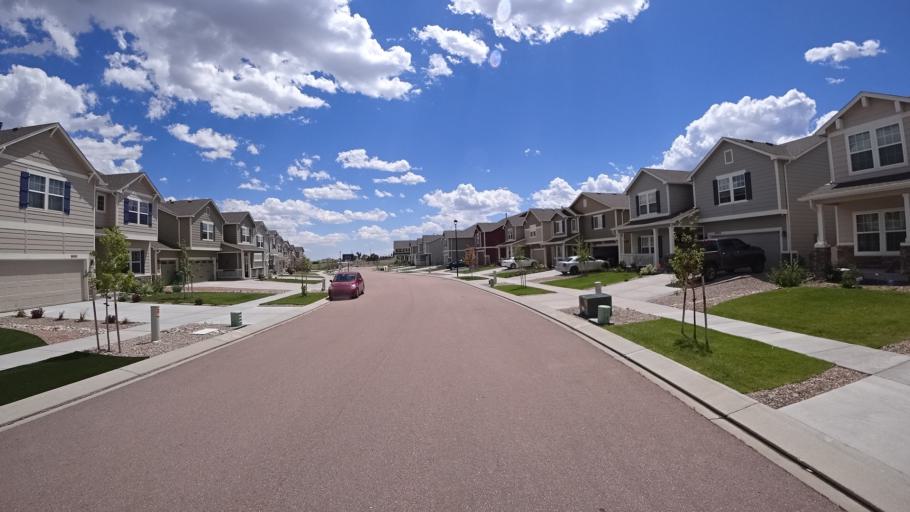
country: US
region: Colorado
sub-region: El Paso County
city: Black Forest
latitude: 38.9503
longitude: -104.7038
